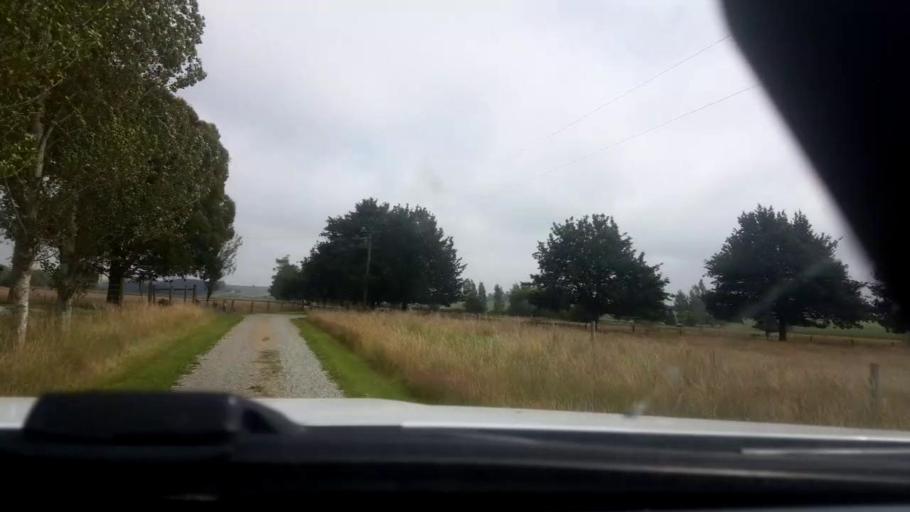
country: NZ
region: Canterbury
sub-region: Timaru District
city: Pleasant Point
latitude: -44.3234
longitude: 171.1934
